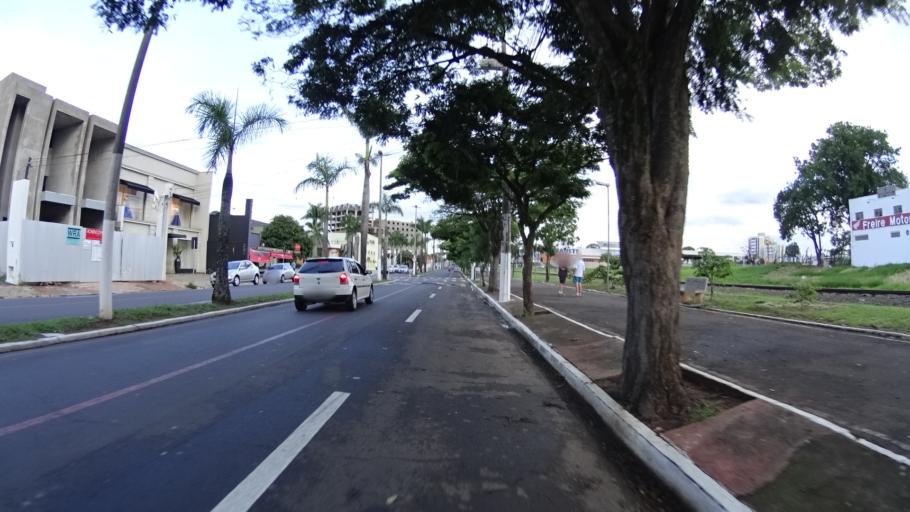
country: BR
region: Sao Paulo
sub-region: Marilia
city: Marilia
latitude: -22.2237
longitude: -49.9349
